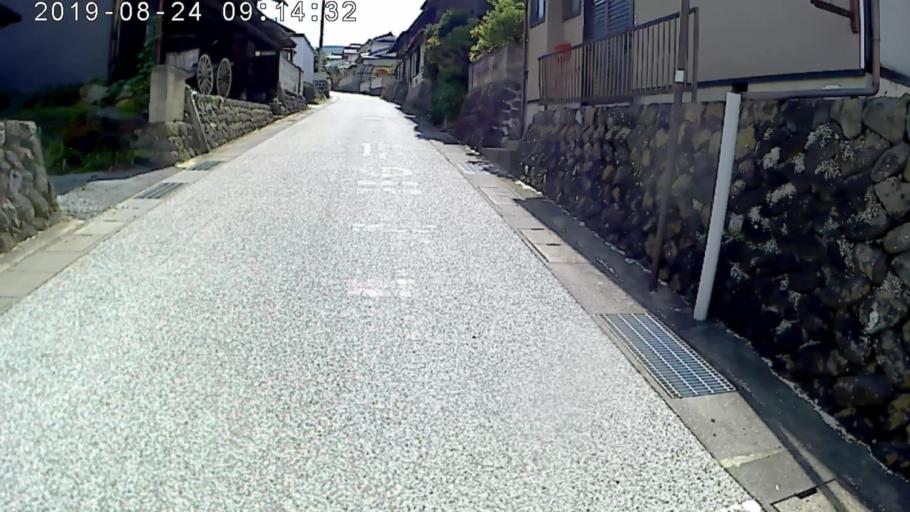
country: JP
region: Nagano
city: Kamimaruko
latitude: 36.2530
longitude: 138.2708
